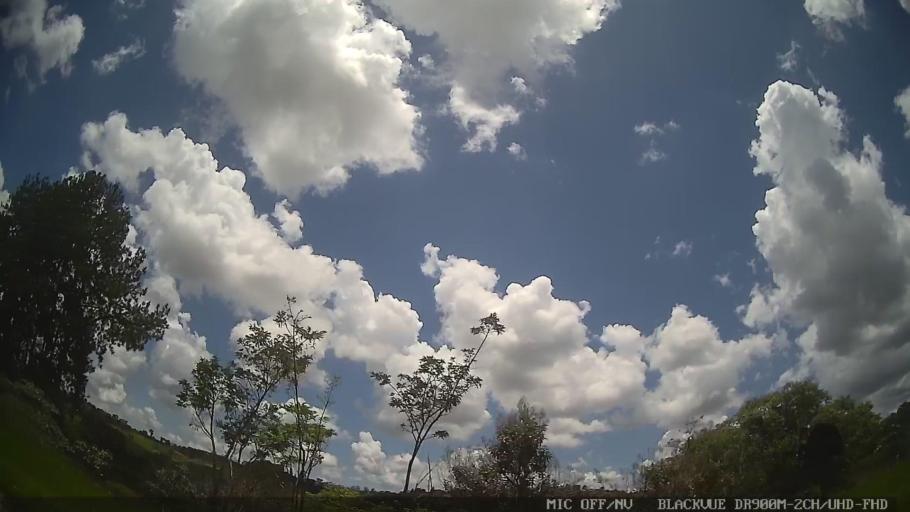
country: BR
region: Sao Paulo
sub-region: Serra Negra
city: Serra Negra
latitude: -22.6273
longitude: -46.7217
